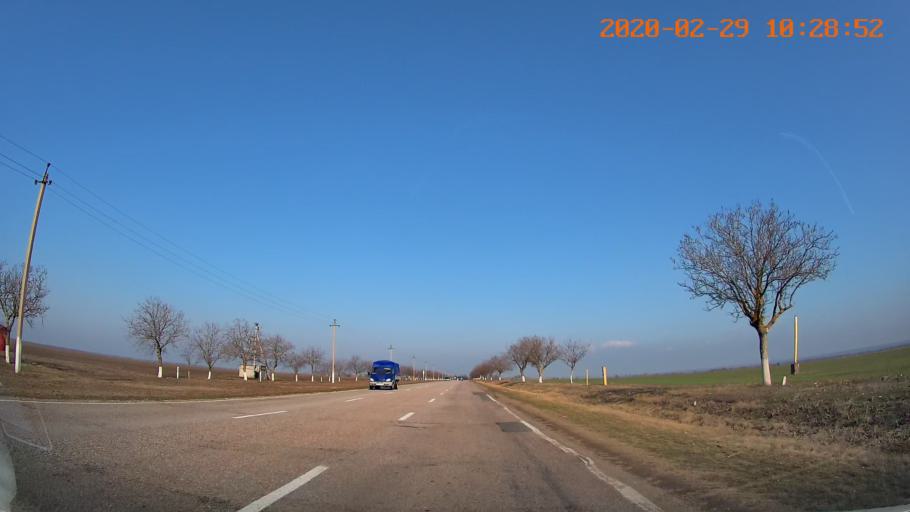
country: MD
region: Telenesti
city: Tiraspolul Nou
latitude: 46.9164
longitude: 29.5889
